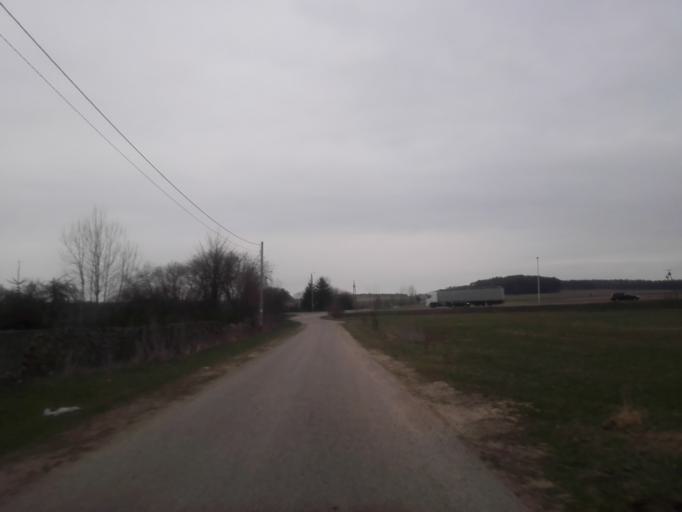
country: PL
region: Podlasie
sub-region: Powiat grajewski
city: Szczuczyn
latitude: 53.4878
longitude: 22.2186
